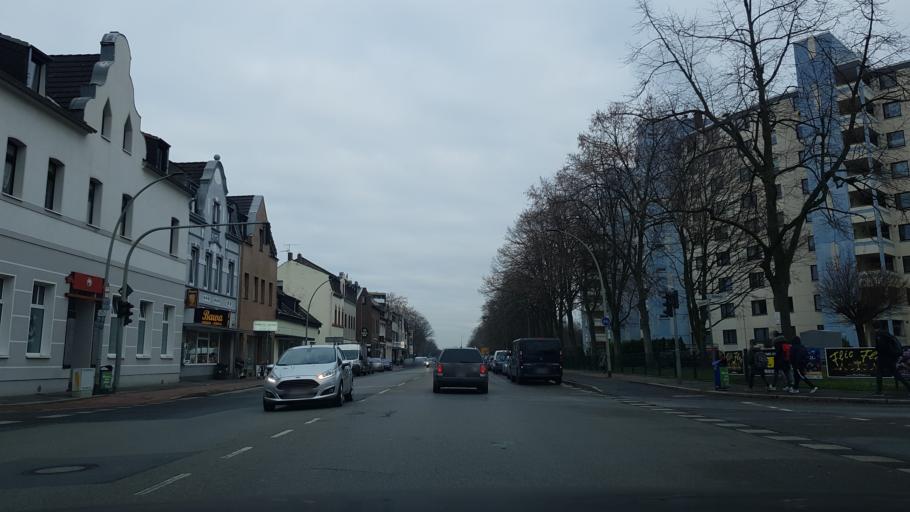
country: DE
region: North Rhine-Westphalia
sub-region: Regierungsbezirk Dusseldorf
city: Moers
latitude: 51.4471
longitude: 6.6897
